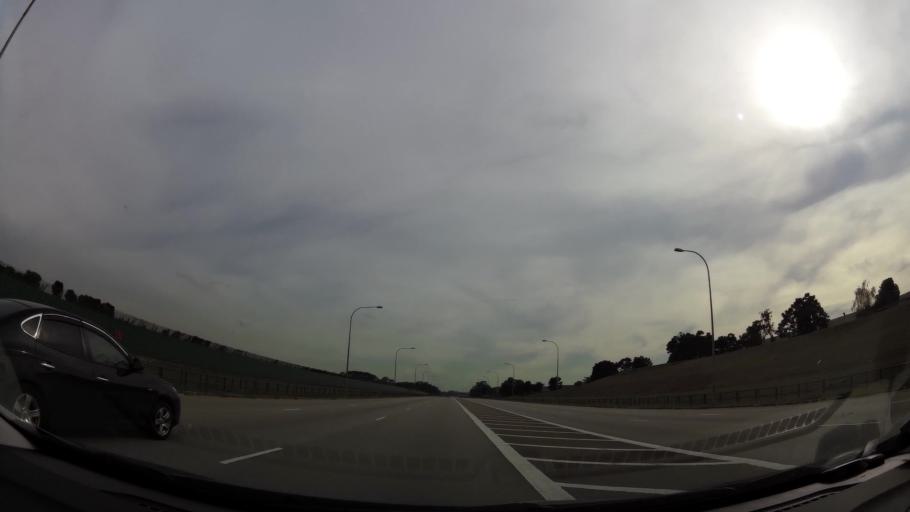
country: MY
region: Johor
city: Johor Bahru
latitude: 1.3903
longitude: 103.6985
